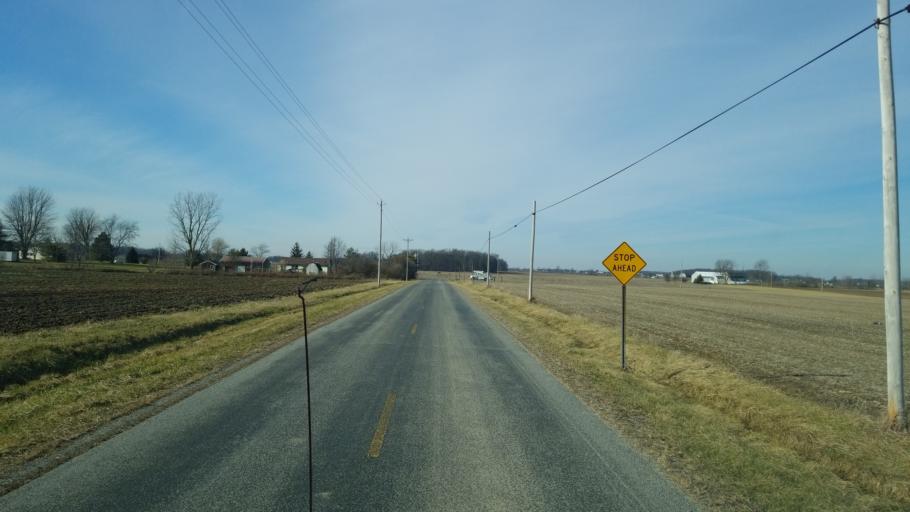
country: US
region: Ohio
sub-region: Hardin County
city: Ada
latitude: 40.8056
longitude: -83.8770
